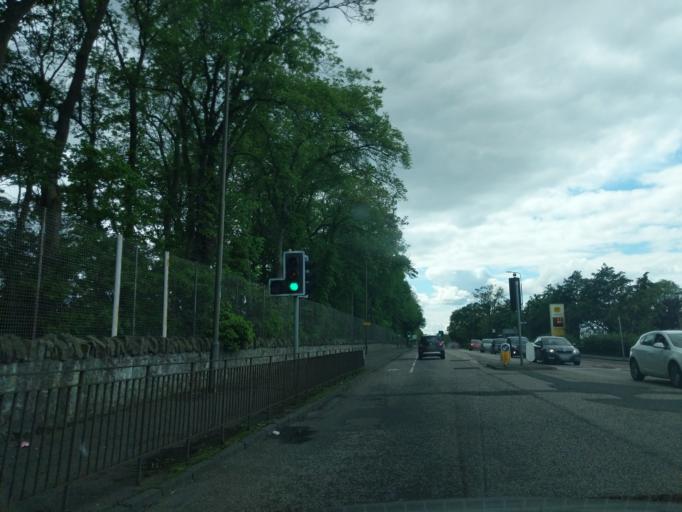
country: GB
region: Scotland
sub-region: Edinburgh
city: Edinburgh
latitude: 55.9692
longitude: -3.2286
